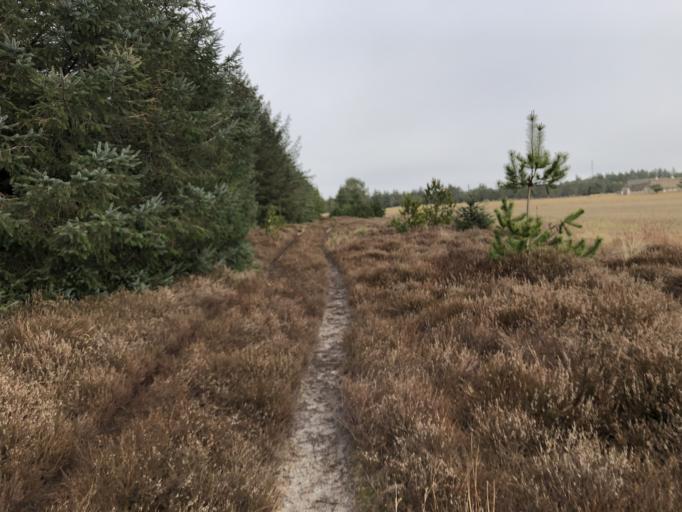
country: DK
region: Central Jutland
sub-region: Holstebro Kommune
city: Ulfborg
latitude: 56.3124
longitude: 8.1372
